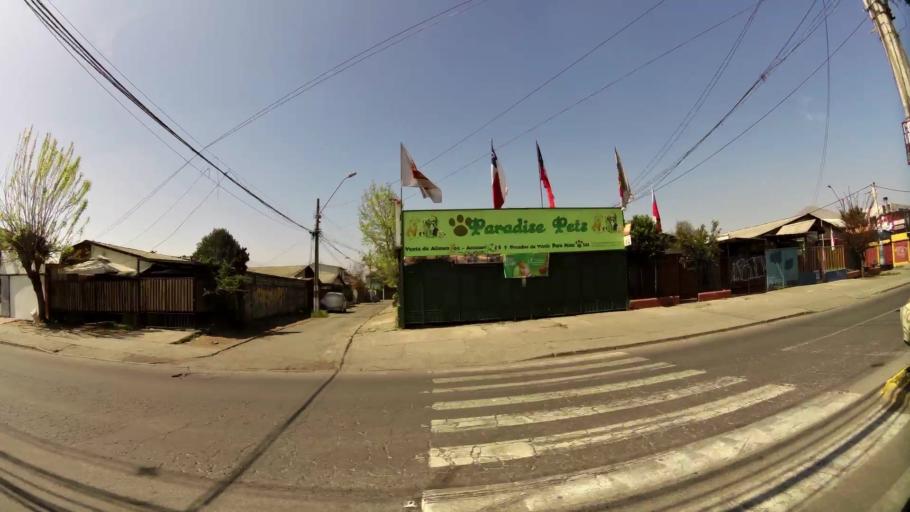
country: CL
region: Santiago Metropolitan
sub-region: Provincia de Santiago
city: Lo Prado
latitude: -33.3640
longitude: -70.7297
